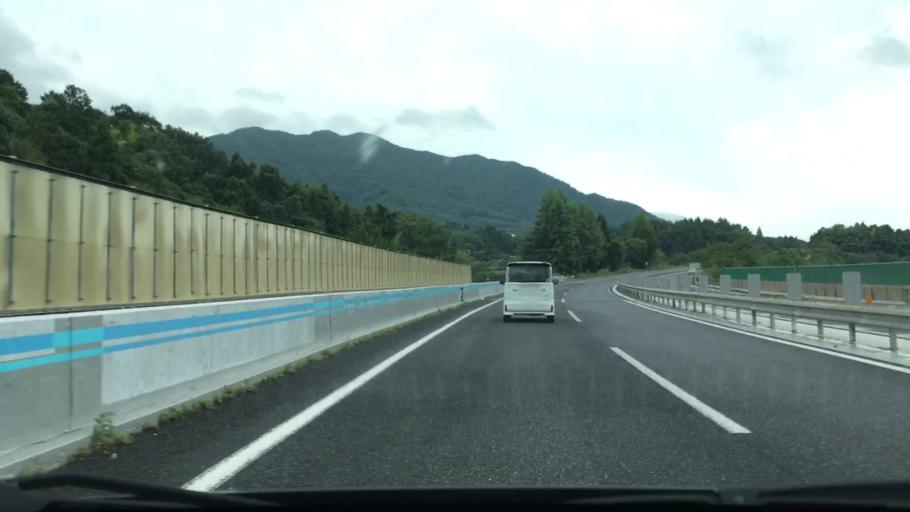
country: JP
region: Hiroshima
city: Hiroshima-shi
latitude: 34.6438
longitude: 132.5172
